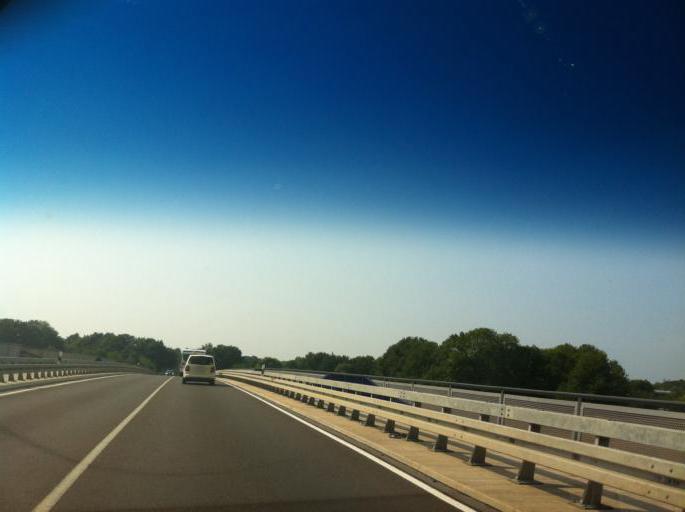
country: DE
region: Saxony
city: Markkleeberg
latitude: 51.2988
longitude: 12.3434
